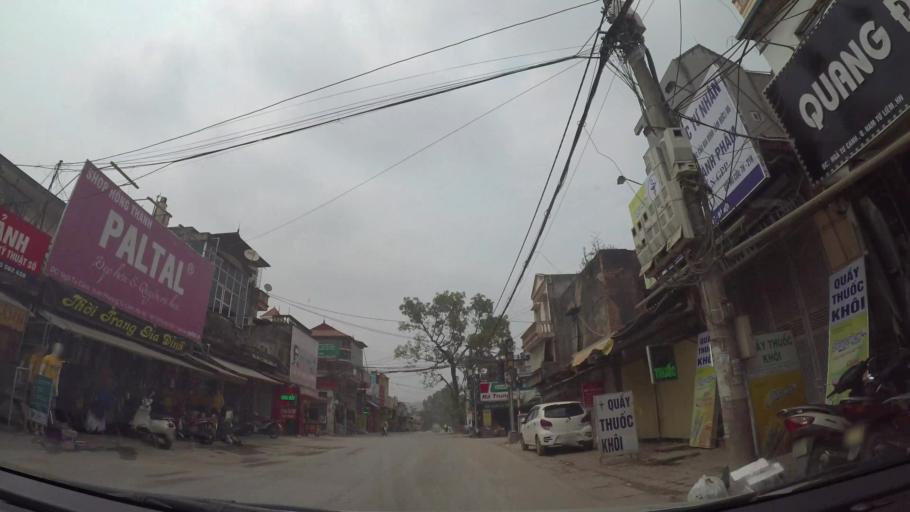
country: VN
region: Ha Noi
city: Cau Dien
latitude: 21.0347
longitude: 105.7386
